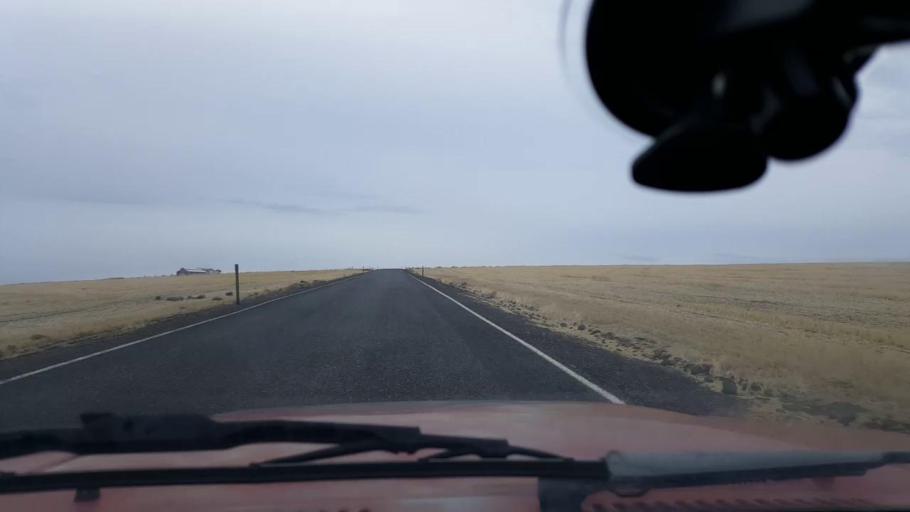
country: US
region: Washington
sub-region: Asotin County
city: Clarkston Heights-Vineland
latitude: 46.3419
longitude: -117.2688
